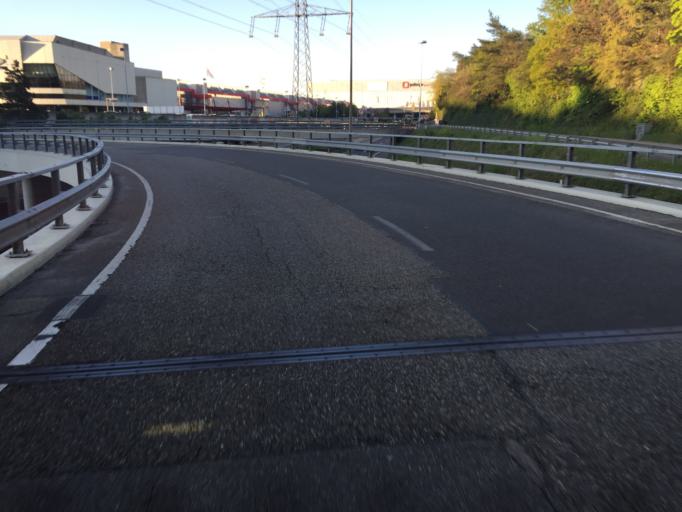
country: CH
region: Geneva
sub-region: Geneva
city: Les Avanchets
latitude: 46.2315
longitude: 6.1121
